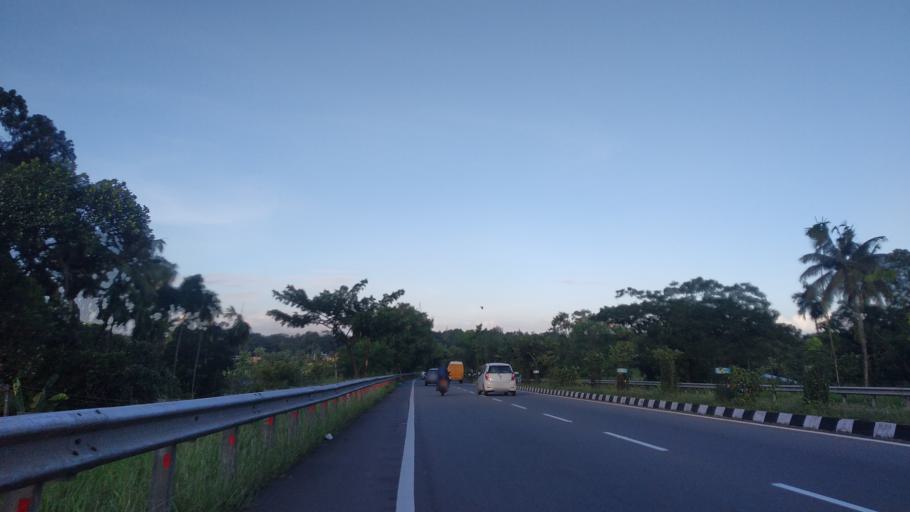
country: IN
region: Kerala
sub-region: Ernakulam
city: Elur
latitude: 10.0677
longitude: 76.2997
